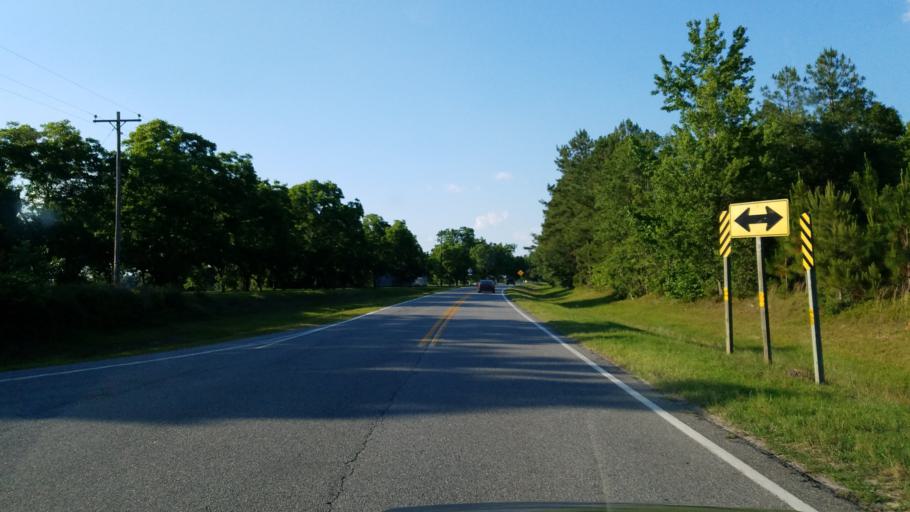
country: US
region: Georgia
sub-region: Lanier County
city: Lakeland
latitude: 30.9702
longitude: -83.0821
